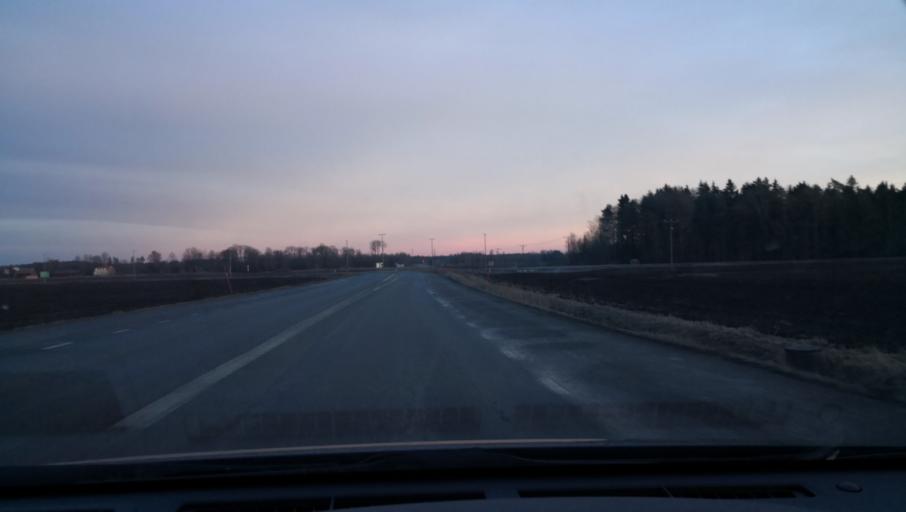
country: SE
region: OErebro
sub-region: Orebro Kommun
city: Vintrosa
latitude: 59.2430
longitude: 15.0481
